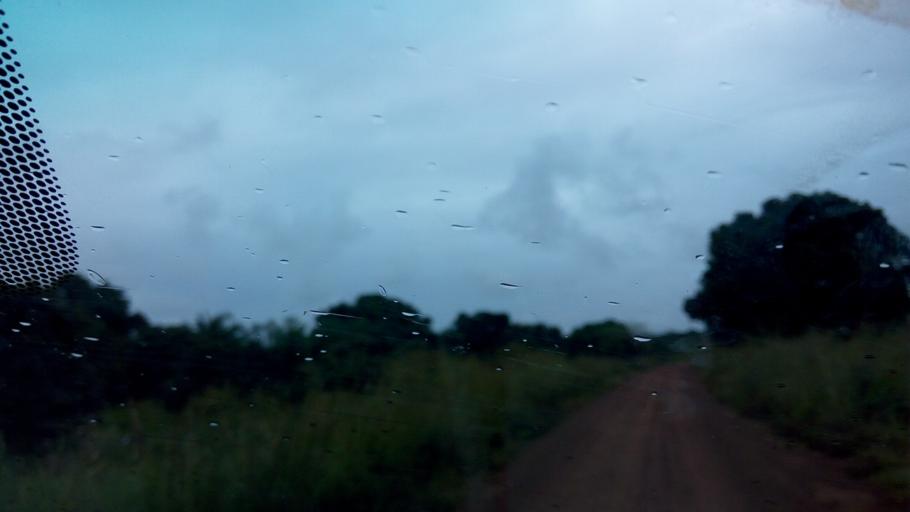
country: ZM
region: Luapula
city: Nchelenge
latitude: -9.0199
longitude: 28.4111
